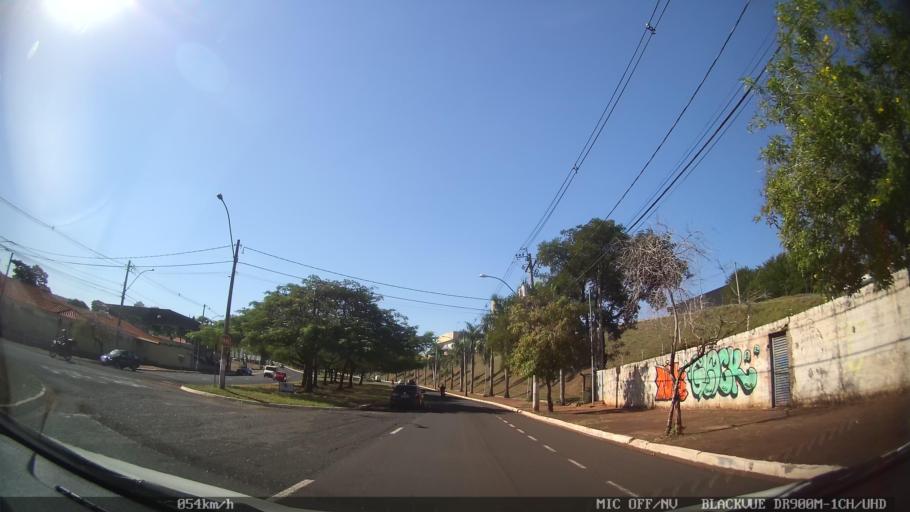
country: BR
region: Sao Paulo
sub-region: Ribeirao Preto
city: Ribeirao Preto
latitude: -21.2101
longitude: -47.7714
